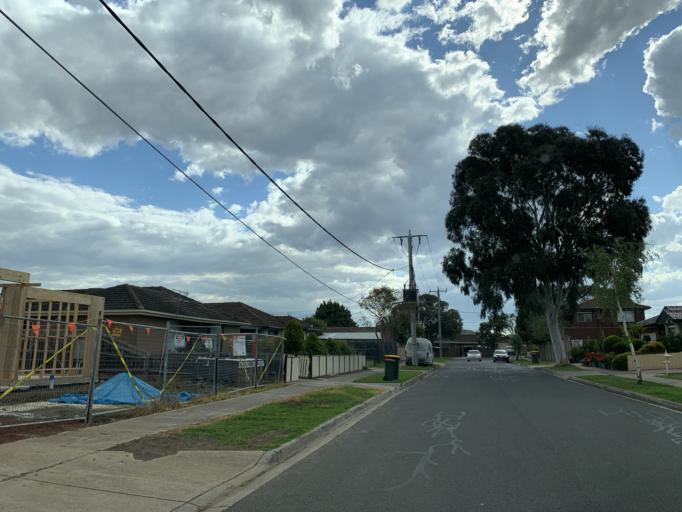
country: AU
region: Victoria
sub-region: Moonee Valley
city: Keilor East
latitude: -37.7444
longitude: 144.8543
